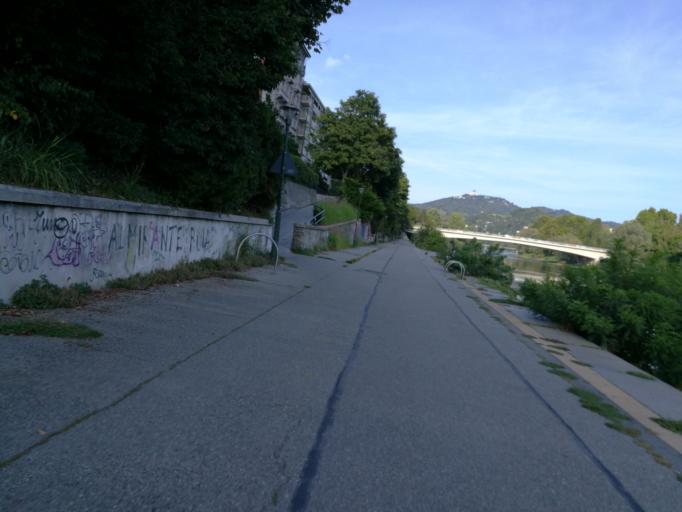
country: IT
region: Piedmont
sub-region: Provincia di Torino
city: Turin
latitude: 45.0676
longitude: 7.7041
